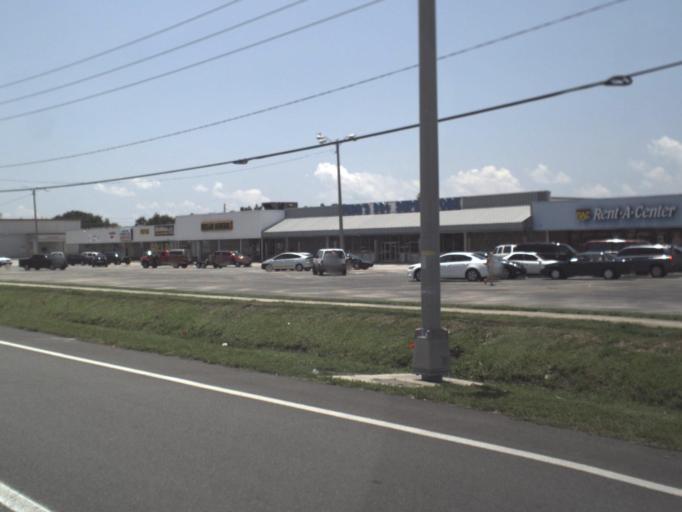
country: US
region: Florida
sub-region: Pasco County
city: Holiday
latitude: 28.1975
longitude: -82.7400
